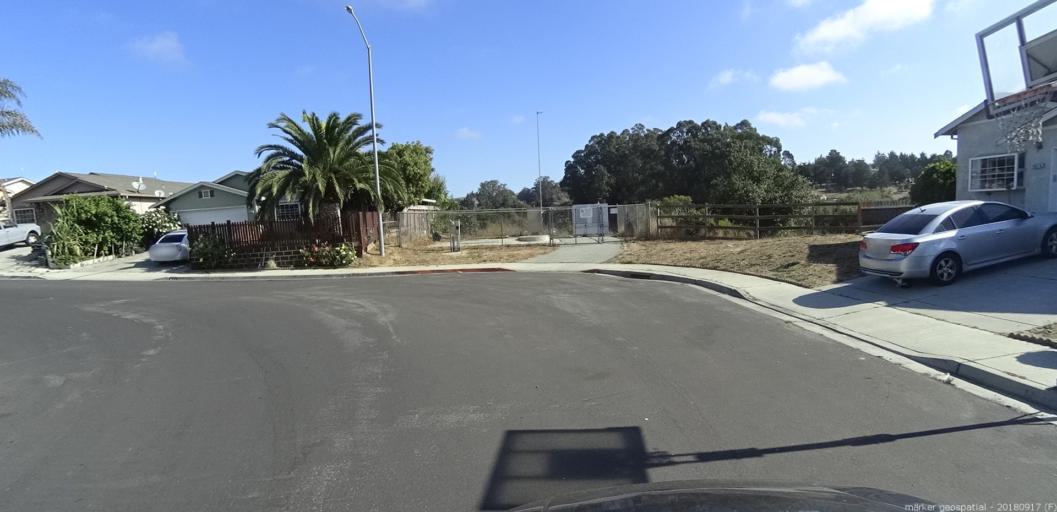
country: US
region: California
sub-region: Monterey County
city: Castroville
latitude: 36.7858
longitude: -121.7261
